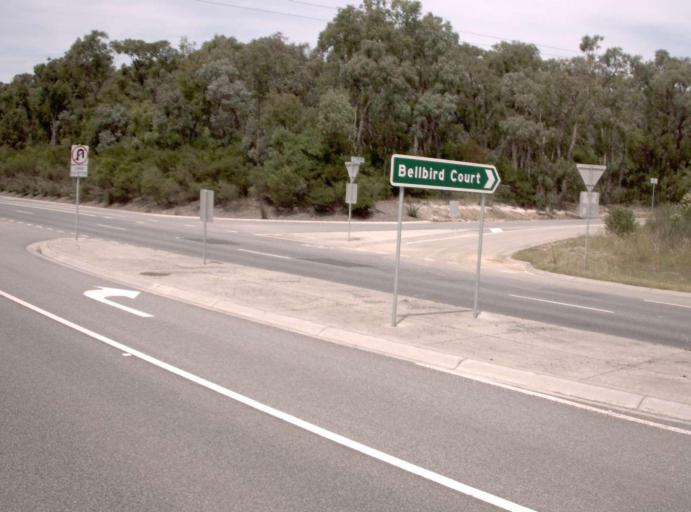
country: AU
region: Victoria
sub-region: Casey
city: Cranbourne South
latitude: -38.1615
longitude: 145.2232
